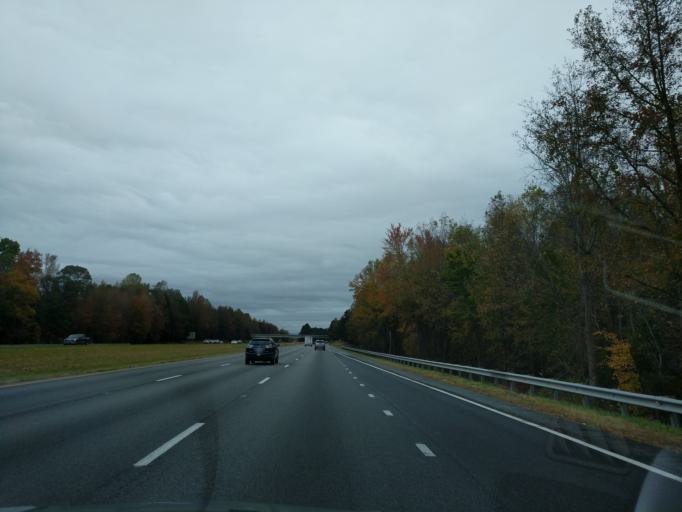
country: US
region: North Carolina
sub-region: Davidson County
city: Lexington
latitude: 35.8138
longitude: -80.1781
